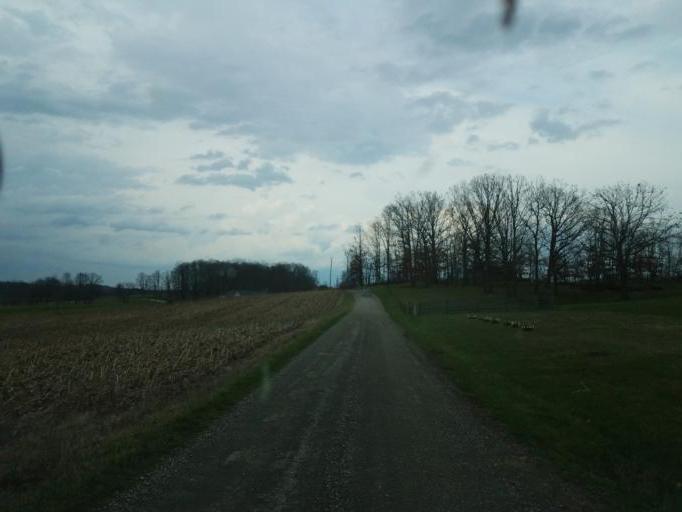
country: US
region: Ohio
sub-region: Muskingum County
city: New Concord
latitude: 40.0852
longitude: -81.8064
